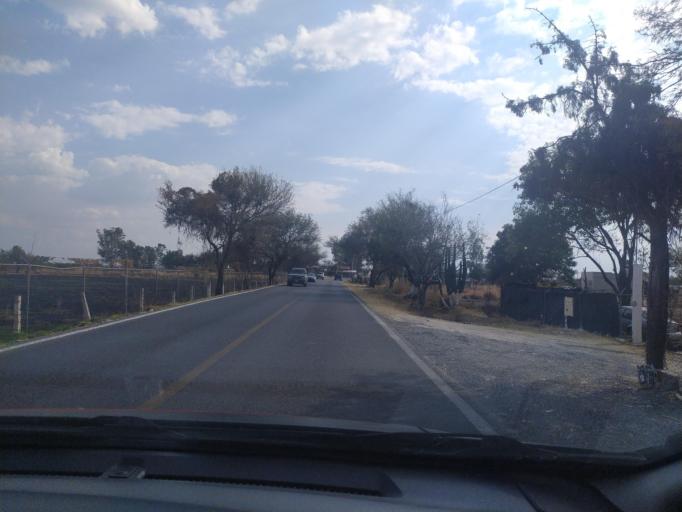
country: MX
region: Guanajuato
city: San Roque
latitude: 20.9735
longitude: -101.8430
